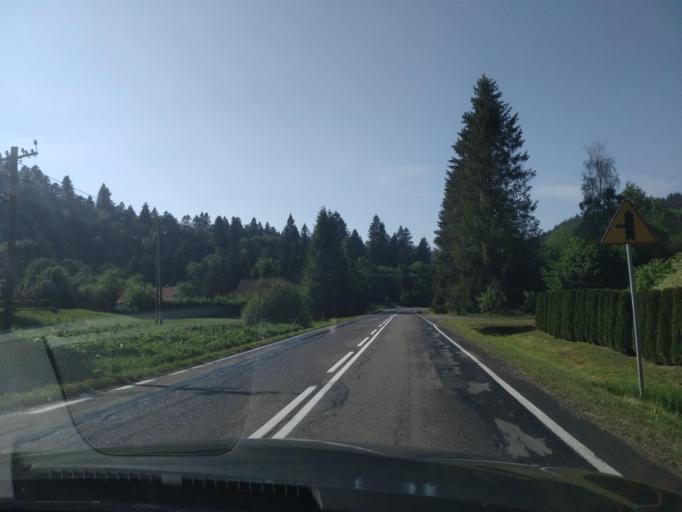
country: PL
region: Subcarpathian Voivodeship
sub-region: Powiat leski
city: Baligrod
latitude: 49.2804
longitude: 22.2804
